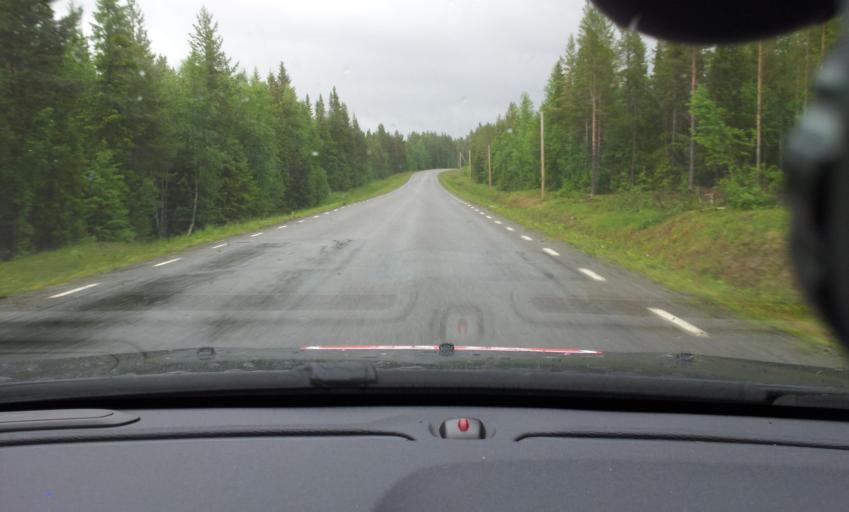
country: SE
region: Jaemtland
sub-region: Are Kommun
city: Are
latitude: 63.1973
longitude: 13.1435
